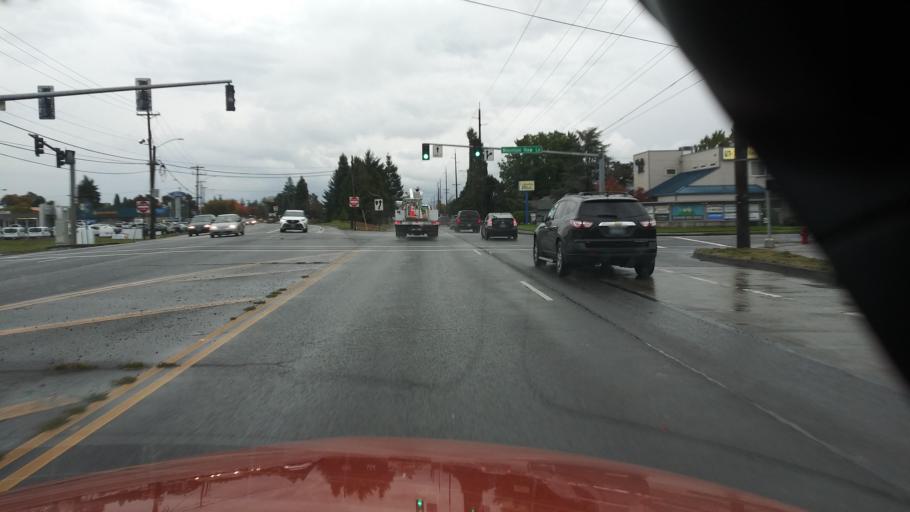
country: US
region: Oregon
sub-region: Washington County
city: Cornelius
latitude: 45.5202
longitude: -123.0765
